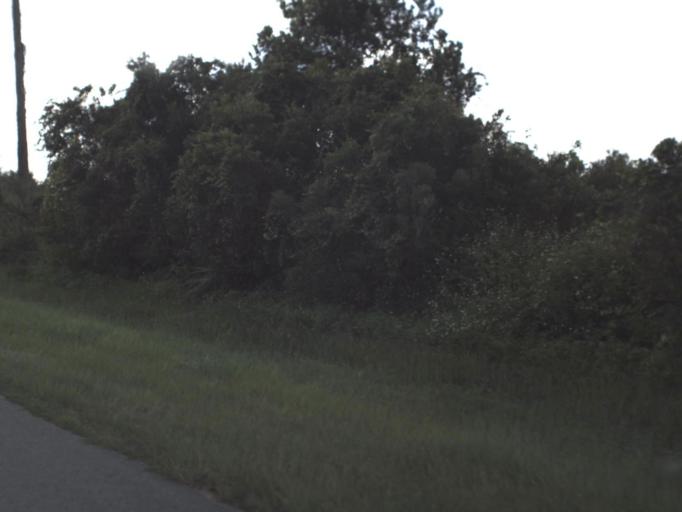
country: US
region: Florida
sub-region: Hillsborough County
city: Wimauma
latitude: 27.4600
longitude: -82.1183
